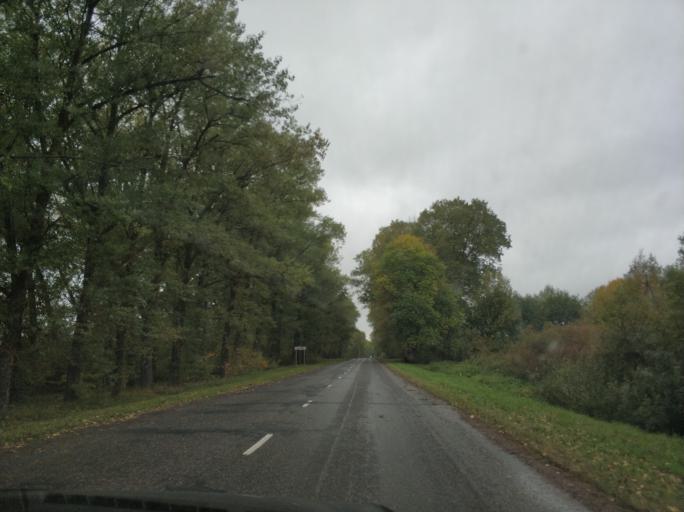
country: BY
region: Vitebsk
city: Polatsk
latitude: 55.4318
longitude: 28.9914
